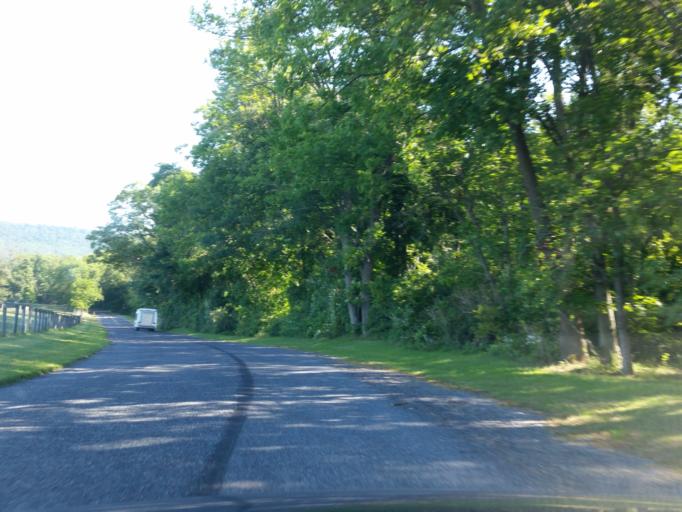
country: US
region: Pennsylvania
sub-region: Lebanon County
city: Palmyra
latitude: 40.4095
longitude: -76.6136
